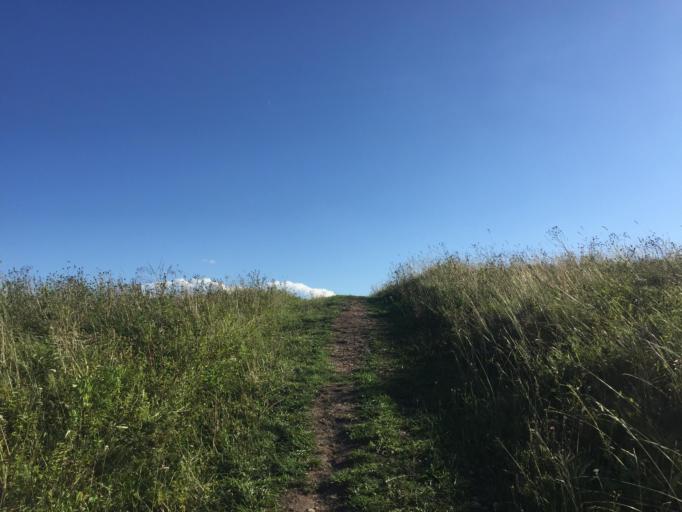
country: RU
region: Leningrad
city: Yelizavetino
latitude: 59.4203
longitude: 29.7721
